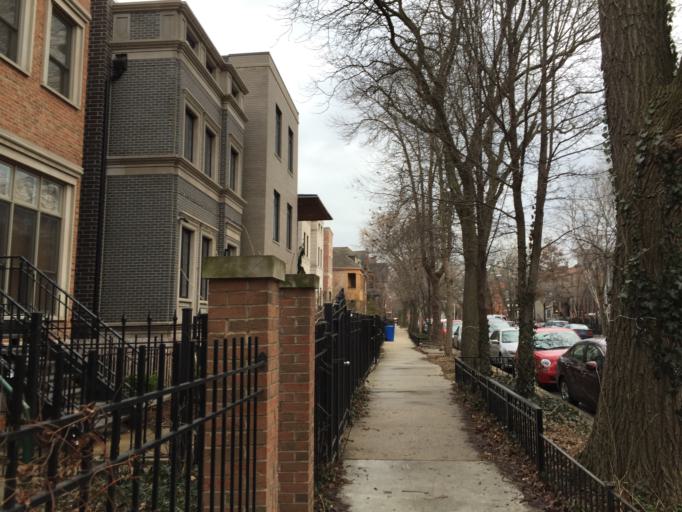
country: US
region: Illinois
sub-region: Cook County
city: Chicago
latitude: 41.9137
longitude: -87.6763
